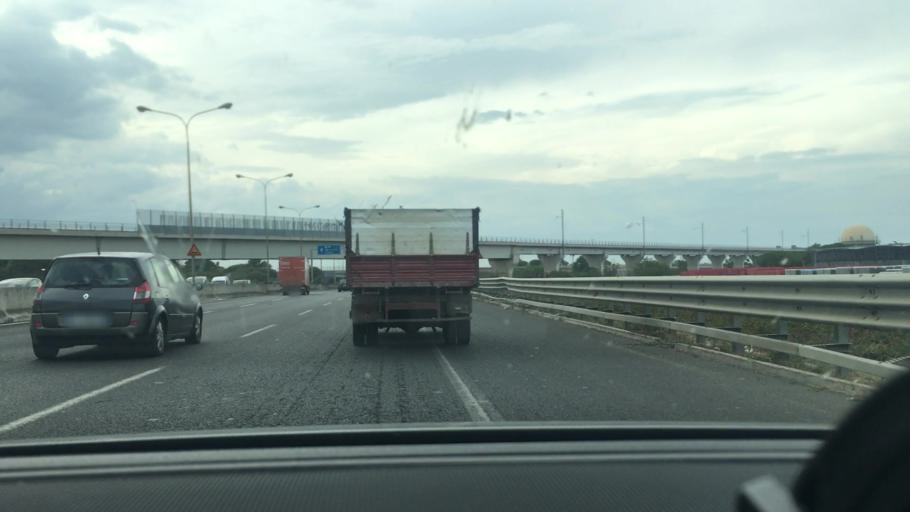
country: IT
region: Apulia
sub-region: Provincia di Bari
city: Bari
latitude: 41.0924
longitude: 16.8454
